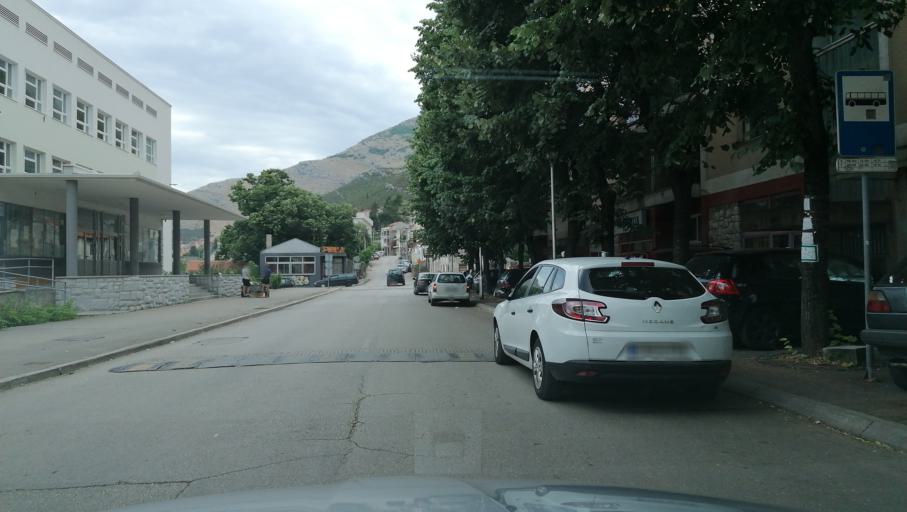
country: BA
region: Republika Srpska
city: Trebinje
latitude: 42.7126
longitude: 18.3408
